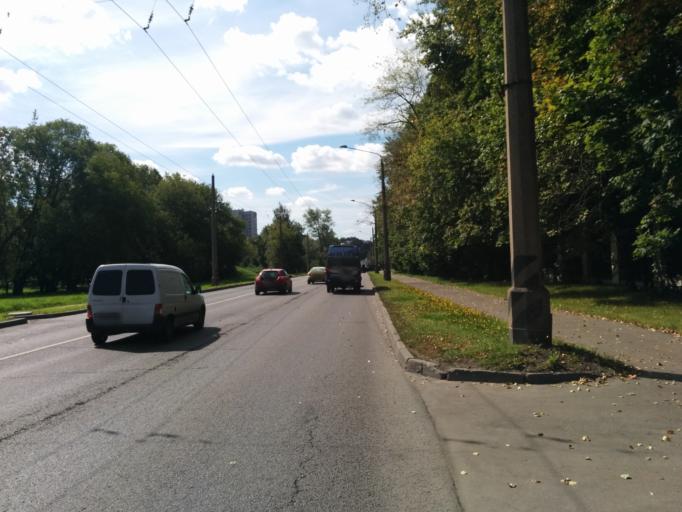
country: RU
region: Moscow
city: Ostankinskiy
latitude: 55.8161
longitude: 37.6176
